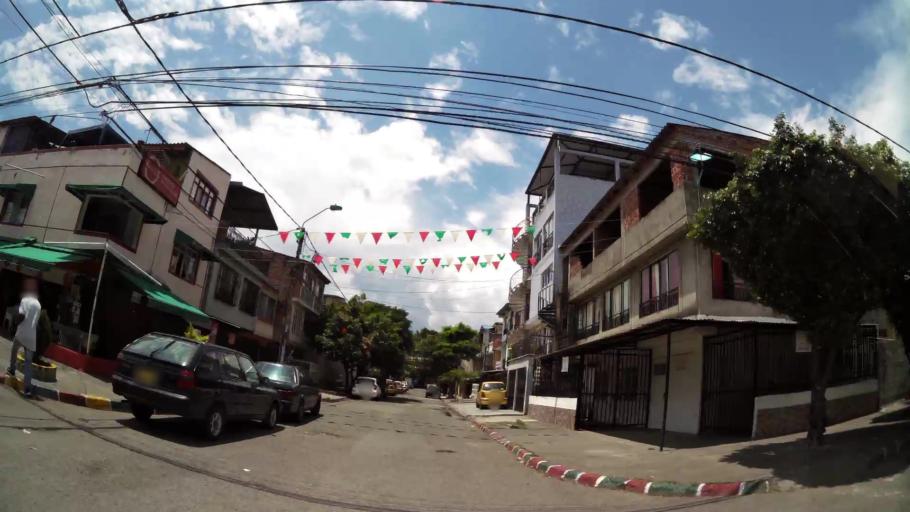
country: CO
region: Valle del Cauca
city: Cali
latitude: 3.4422
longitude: -76.5049
